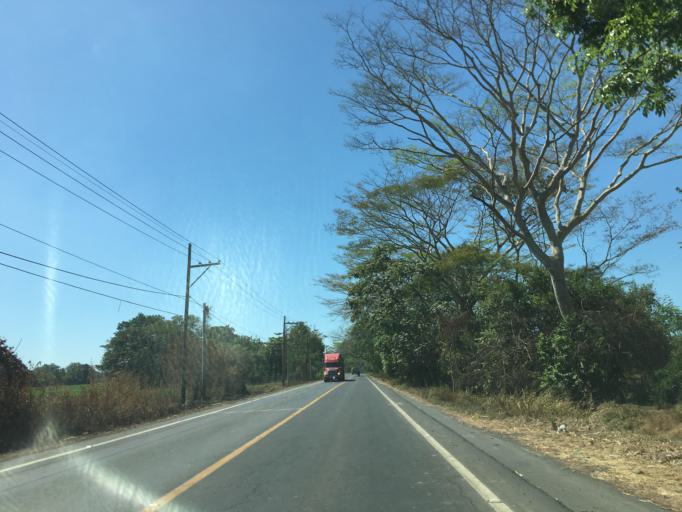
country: GT
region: Escuintla
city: Puerto San Jose
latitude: 13.9996
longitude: -90.8942
